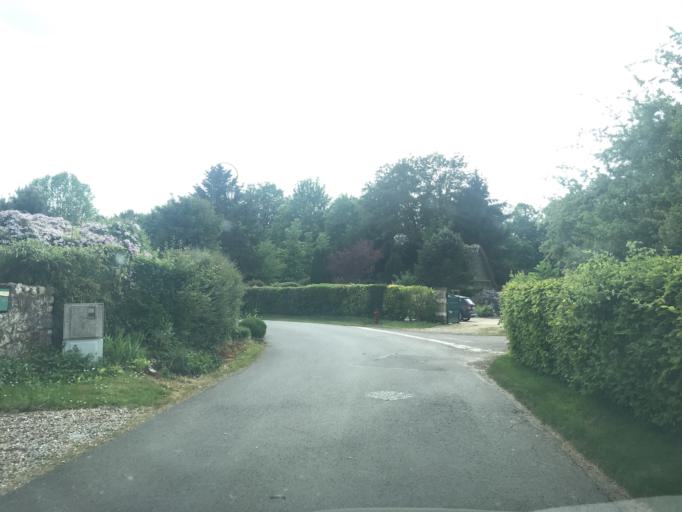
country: FR
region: Haute-Normandie
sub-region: Departement de l'Eure
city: Nassandres
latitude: 49.1707
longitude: 0.7857
